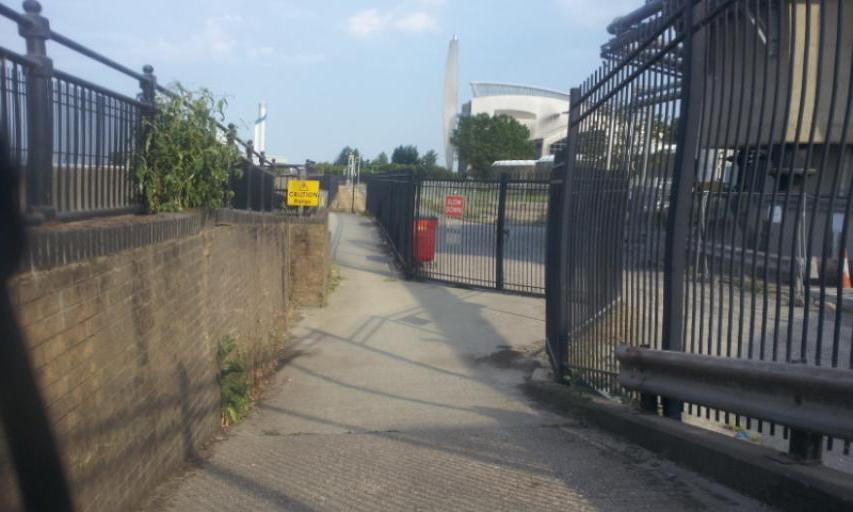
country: GB
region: England
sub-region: Greater London
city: Belvedere
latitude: 51.5076
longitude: 0.1441
